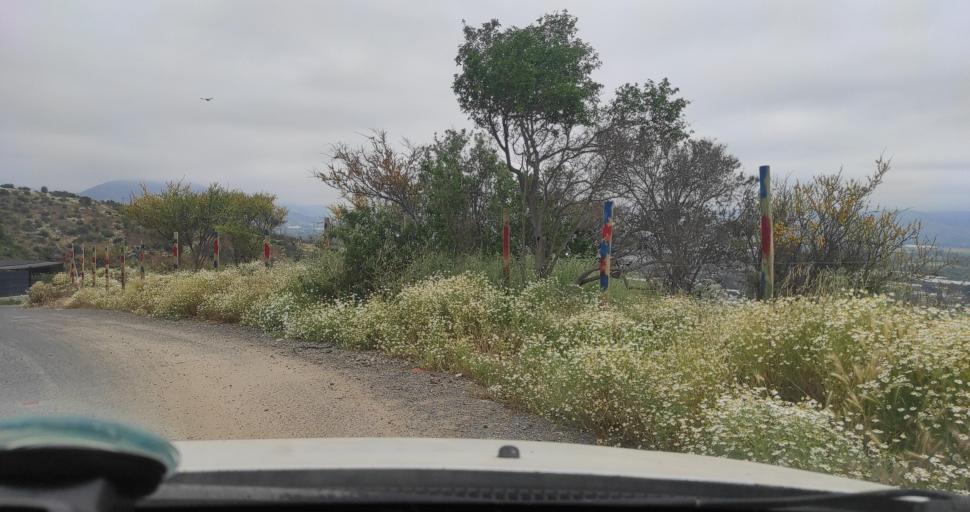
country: CL
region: Valparaiso
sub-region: Provincia de Marga Marga
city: Limache
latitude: -32.9831
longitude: -71.2251
